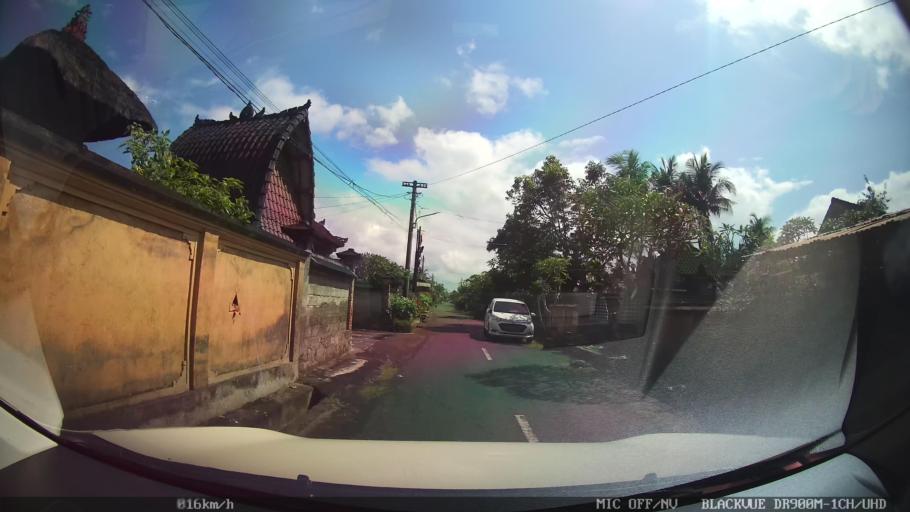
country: ID
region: Bali
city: Banjar Sedang
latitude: -8.5610
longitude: 115.2688
